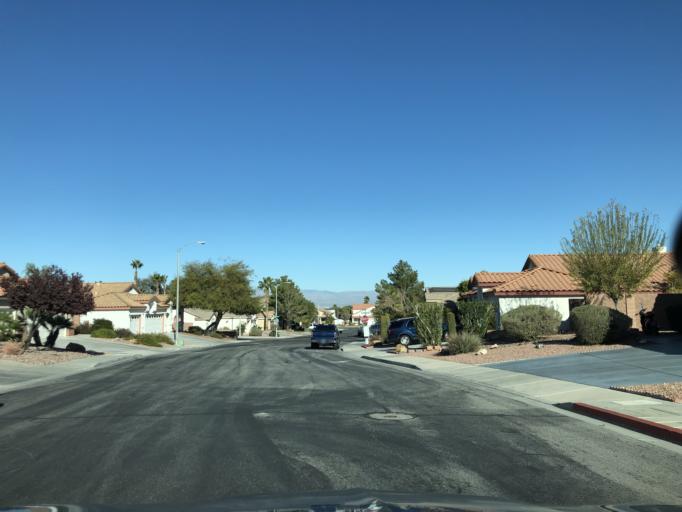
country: US
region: Nevada
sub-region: Clark County
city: Whitney
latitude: 36.0090
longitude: -115.0853
